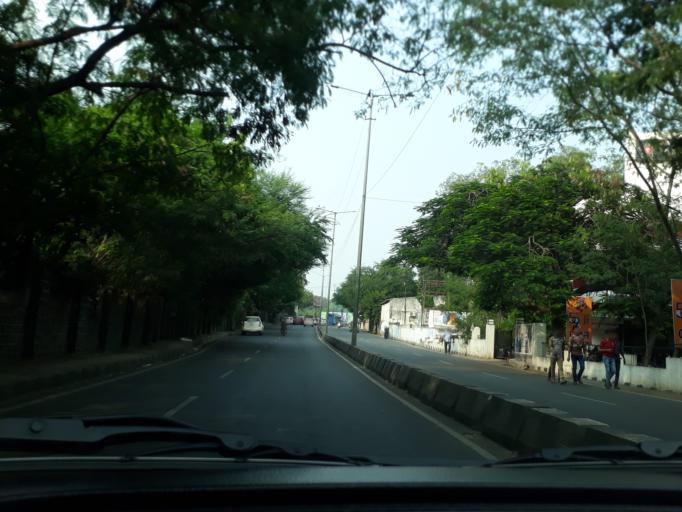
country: IN
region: Telangana
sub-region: Hyderabad
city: Malkajgiri
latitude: 17.4469
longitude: 78.4919
